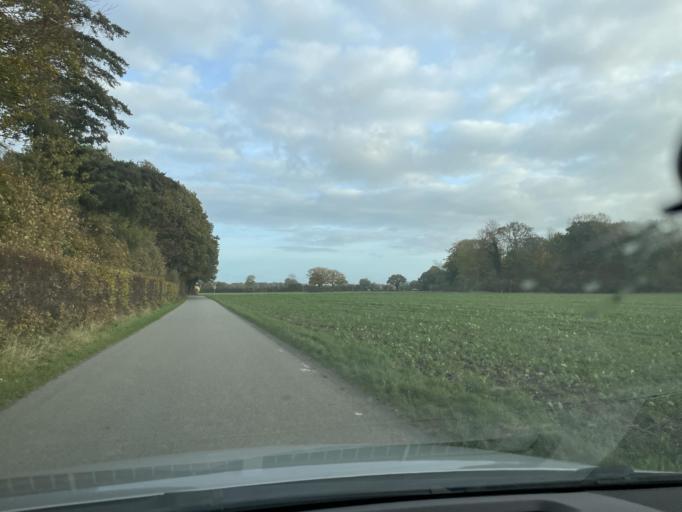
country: DK
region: South Denmark
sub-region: Kerteminde Kommune
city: Kerteminde
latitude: 55.4206
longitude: 10.6770
